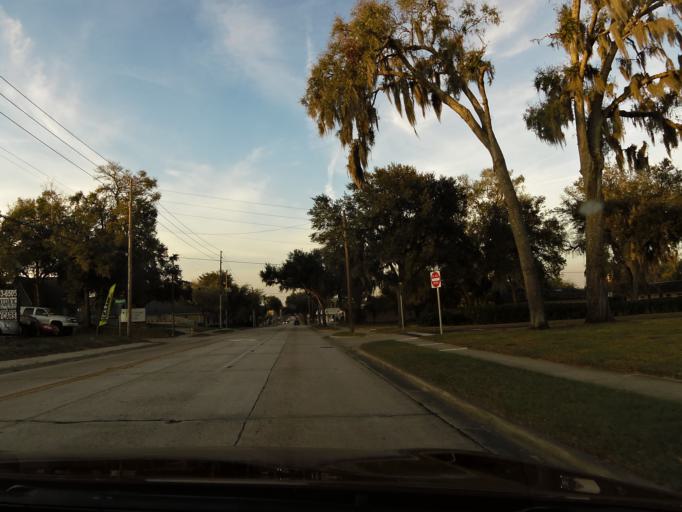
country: US
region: Florida
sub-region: Volusia County
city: DeLand
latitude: 29.0169
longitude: -81.3030
